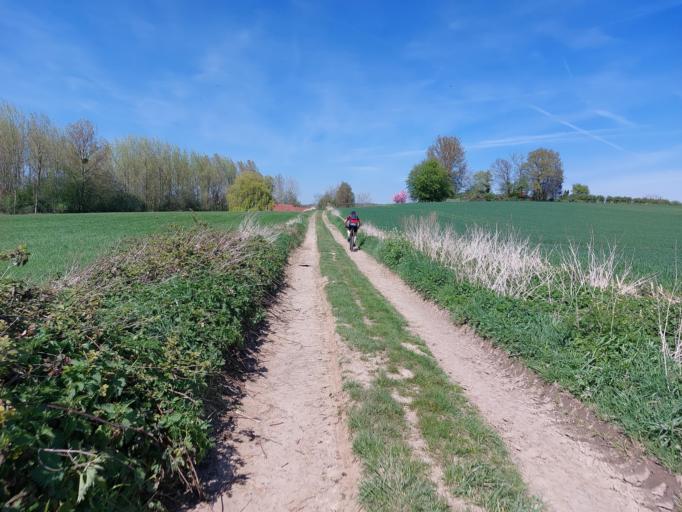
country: BE
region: Wallonia
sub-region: Province du Hainaut
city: Silly
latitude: 50.6054
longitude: 3.9735
